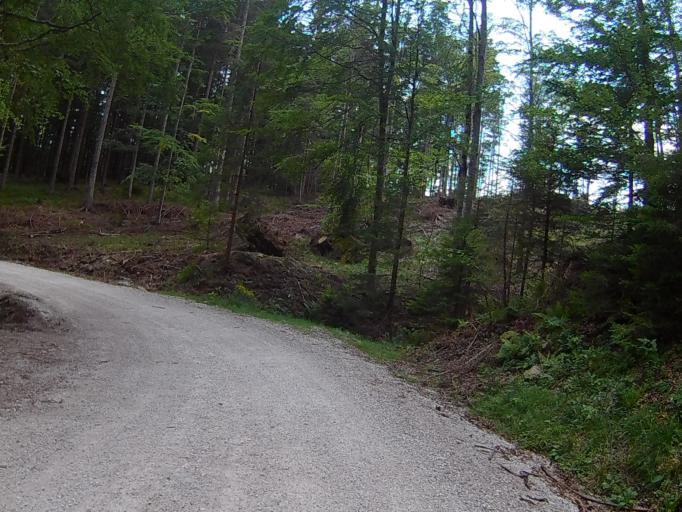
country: SI
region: Lovrenc na Pohorju
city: Lovrenc na Pohorju
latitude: 46.4835
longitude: 15.4439
